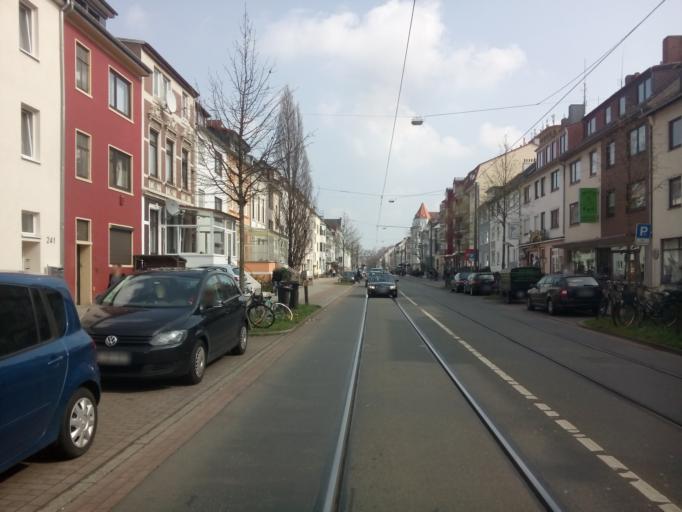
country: DE
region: Bremen
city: Bremen
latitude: 53.0690
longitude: 8.7858
